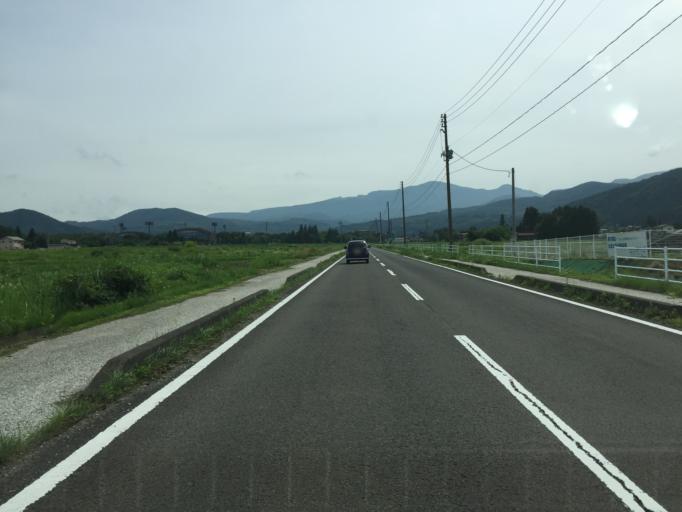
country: JP
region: Fukushima
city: Fukushima-shi
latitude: 37.7316
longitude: 140.3668
